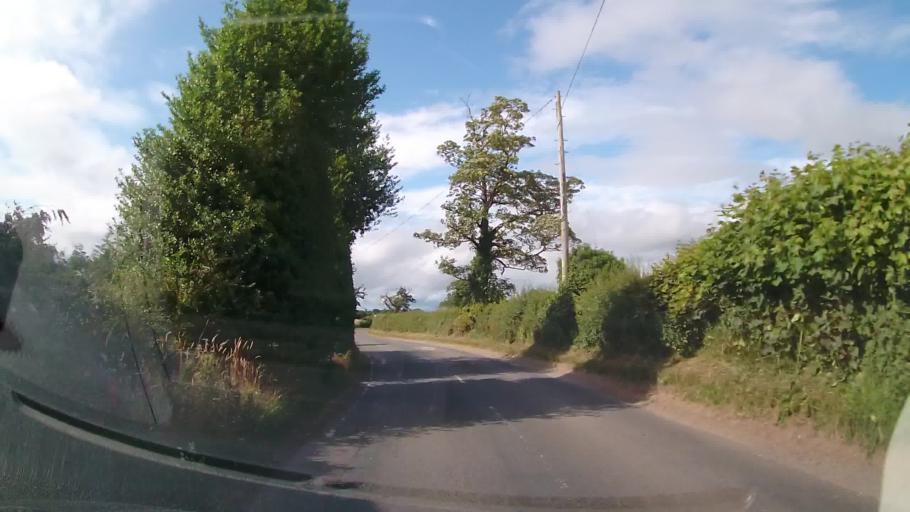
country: GB
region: England
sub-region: Shropshire
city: Petton
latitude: 52.8406
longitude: -2.8045
